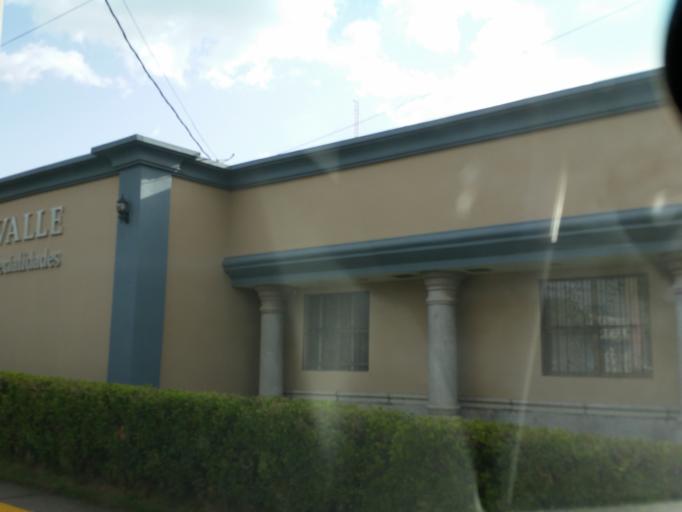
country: NI
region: Managua
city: Managua
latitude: 12.1213
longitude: -86.2526
